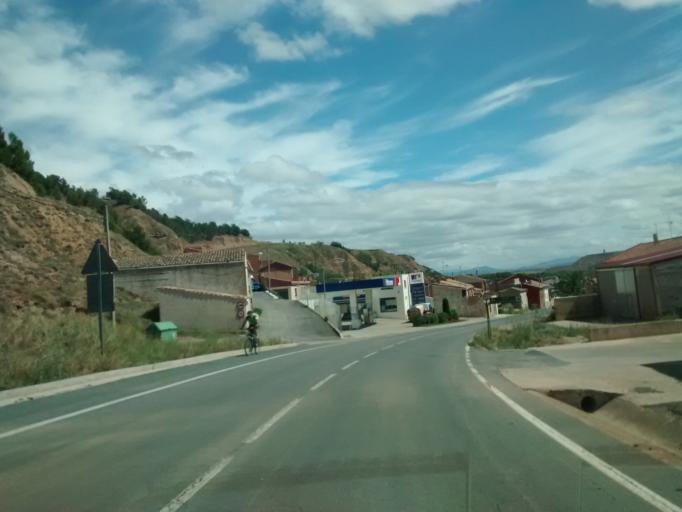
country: ES
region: La Rioja
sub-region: Provincia de La Rioja
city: Murillo de Rio Leza
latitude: 42.3988
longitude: -2.3344
